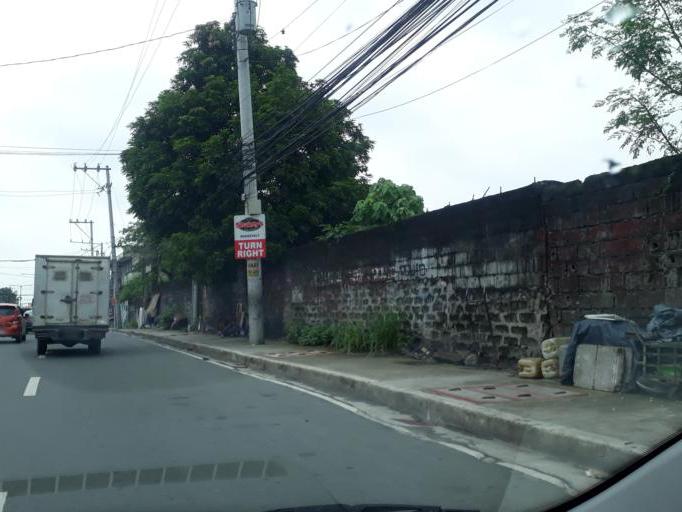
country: PH
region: Calabarzon
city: Del Monte
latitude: 14.6420
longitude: 121.0166
